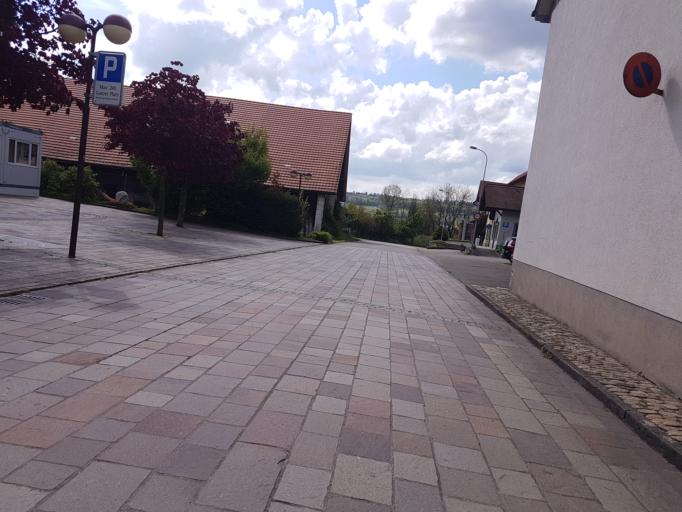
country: CH
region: Solothurn
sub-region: Bezirk Olten
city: Gunzgen
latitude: 47.3090
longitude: 7.8564
